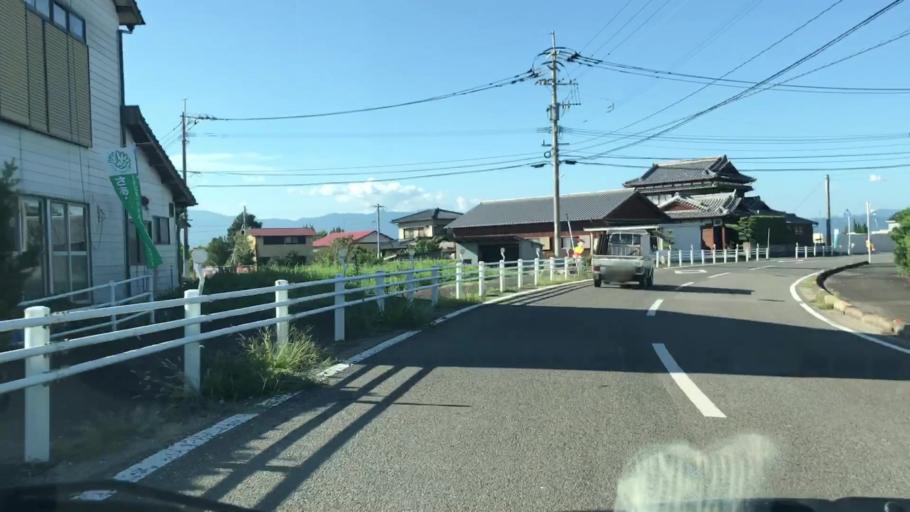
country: JP
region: Saga Prefecture
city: Saga-shi
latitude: 33.2015
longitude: 130.2656
